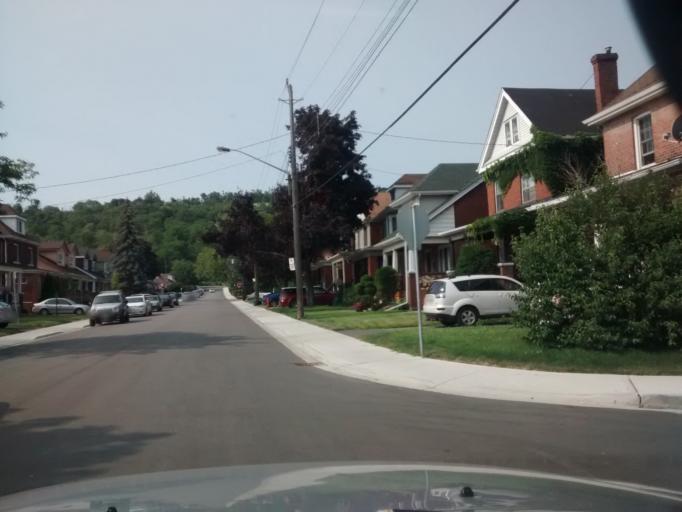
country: CA
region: Ontario
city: Hamilton
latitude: 43.2371
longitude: -79.8220
